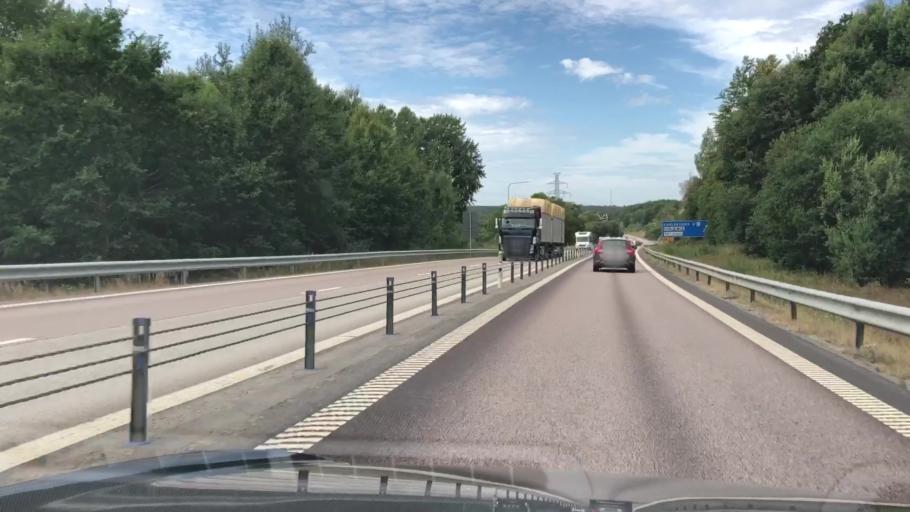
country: SE
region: Blekinge
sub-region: Karlskrona Kommun
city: Rodeby
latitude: 56.2100
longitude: 15.6077
